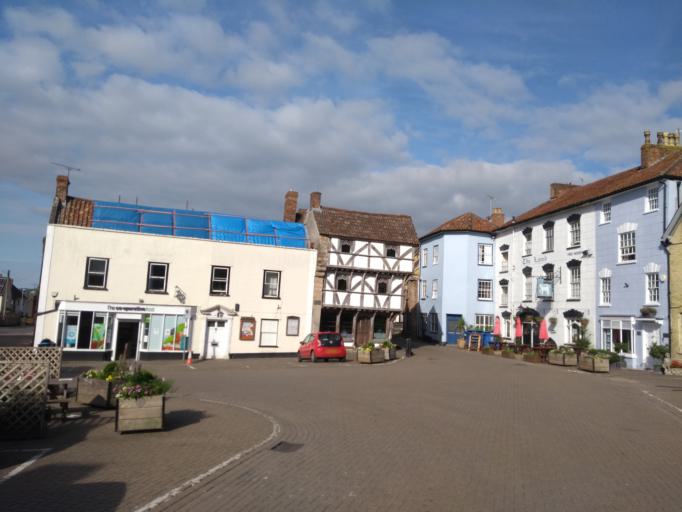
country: GB
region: England
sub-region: Somerset
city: Axbridge
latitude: 51.2872
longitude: -2.8172
